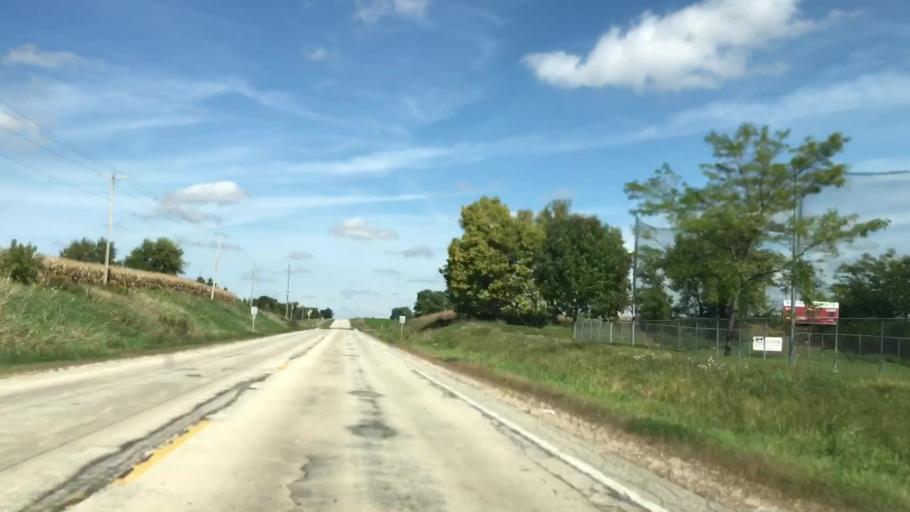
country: US
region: Wisconsin
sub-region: Dodge County
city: Mayville
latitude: 43.4989
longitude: -88.5710
